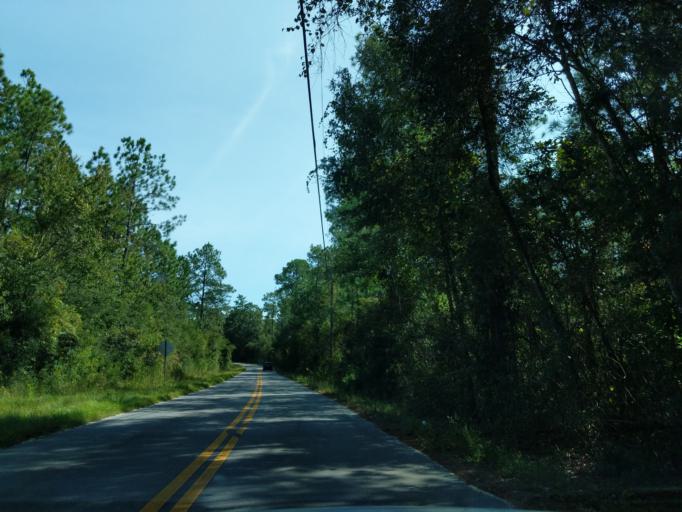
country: US
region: Florida
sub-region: Okaloosa County
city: Crestview
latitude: 30.7074
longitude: -86.5964
